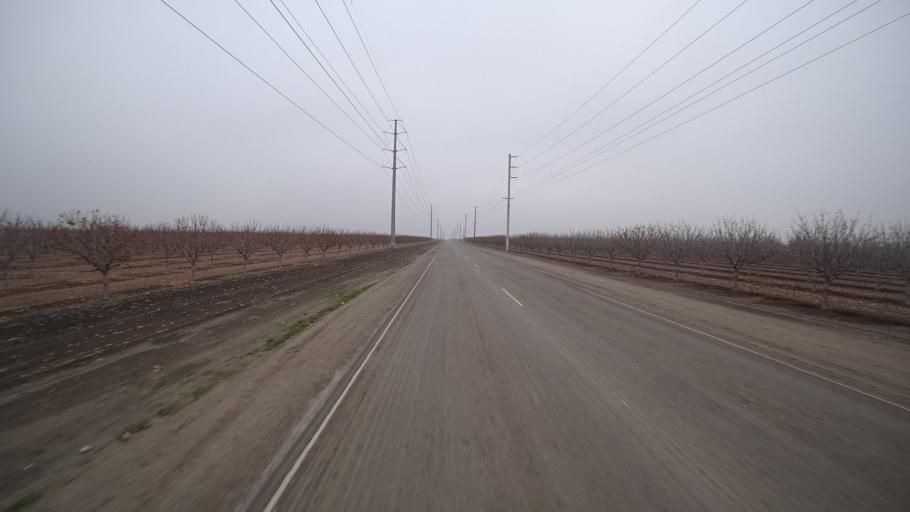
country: US
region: California
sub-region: Kern County
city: Buttonwillow
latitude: 35.3868
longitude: -119.4476
